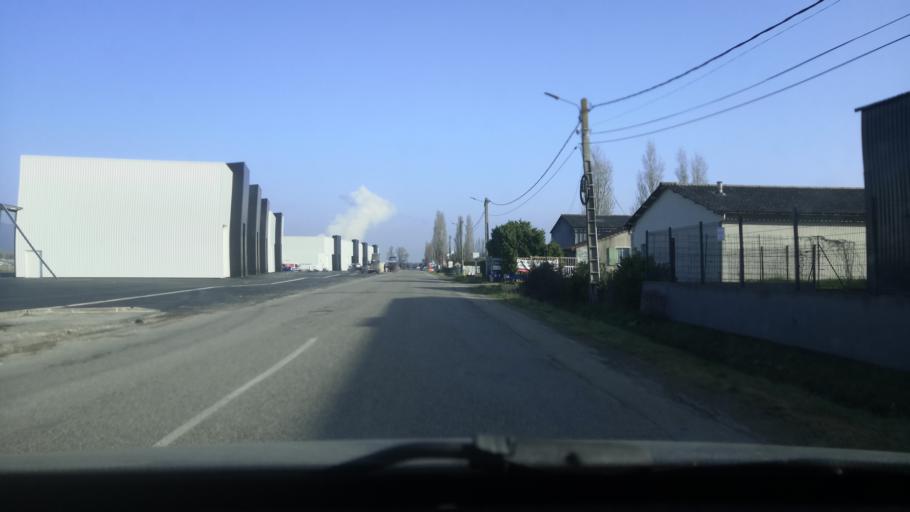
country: FR
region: Rhone-Alpes
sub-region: Departement de la Drome
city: Ancone
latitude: 44.5730
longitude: 4.7386
